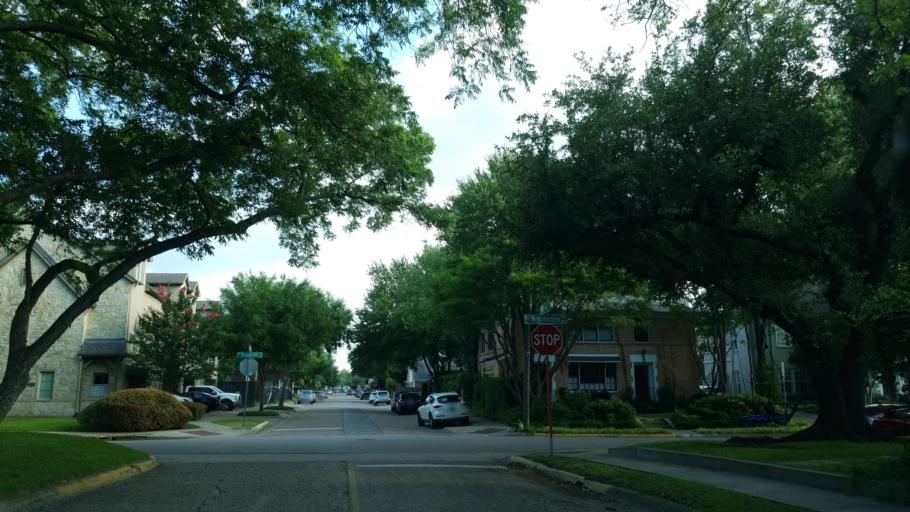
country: US
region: Texas
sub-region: Dallas County
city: University Park
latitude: 32.8505
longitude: -96.7892
